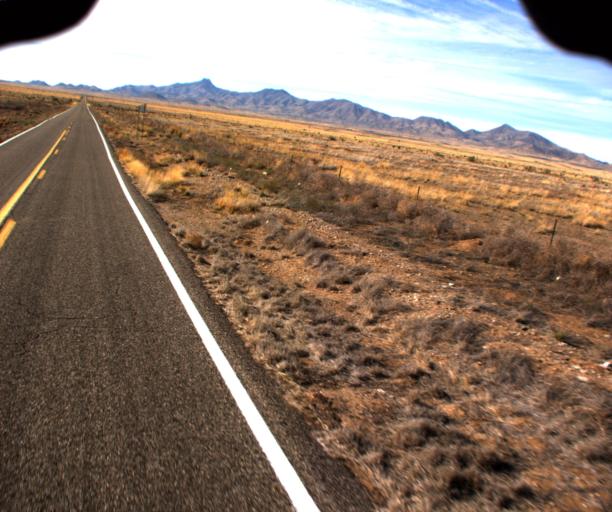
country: US
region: Arizona
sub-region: Cochise County
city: Willcox
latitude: 32.0632
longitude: -109.5041
